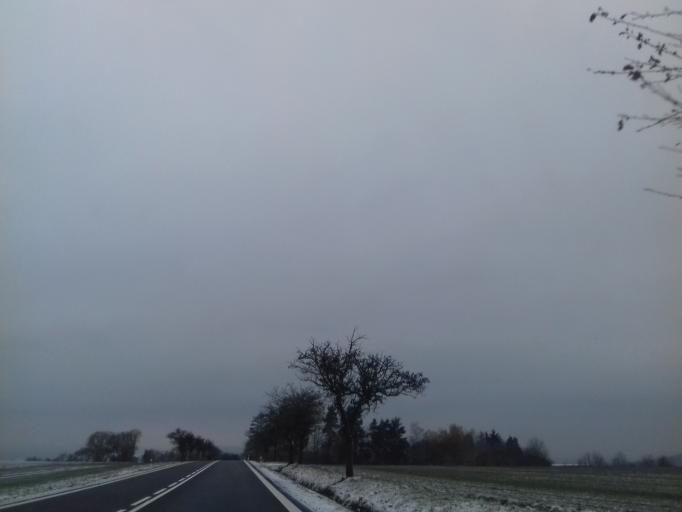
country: CZ
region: Plzensky
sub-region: Okres Domazlice
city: Domazlice
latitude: 49.4497
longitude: 12.8885
